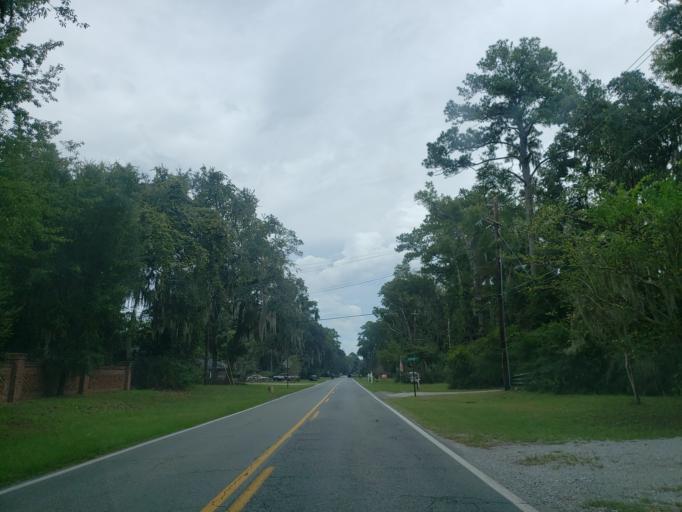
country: US
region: Georgia
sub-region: Chatham County
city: Wilmington Island
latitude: 32.0014
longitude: -80.9685
